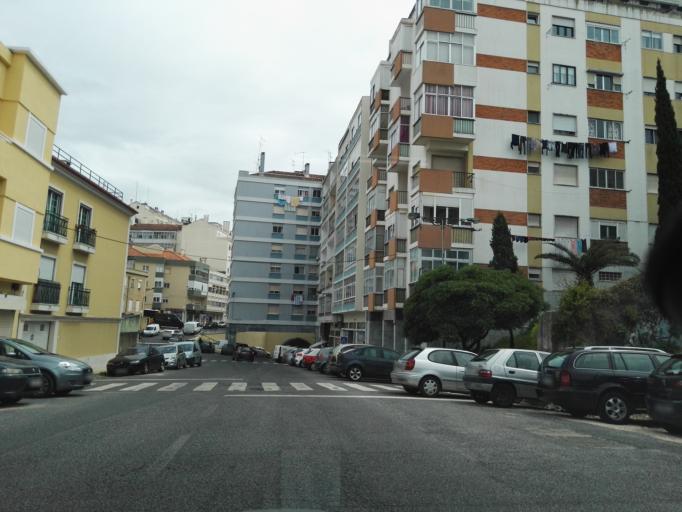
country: PT
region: Setubal
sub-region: Almada
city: Pragal
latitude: 38.7044
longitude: -9.1918
